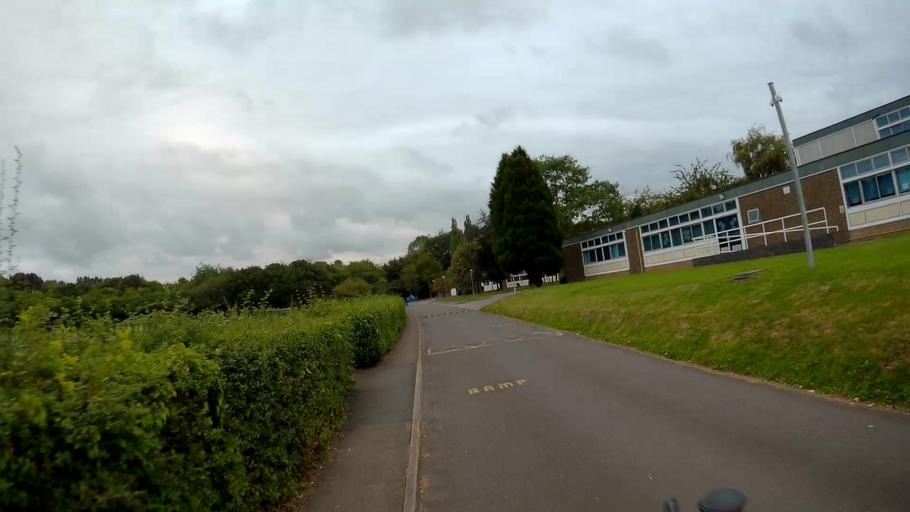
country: GB
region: England
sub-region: Hampshire
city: Basingstoke
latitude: 51.2556
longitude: -1.0986
